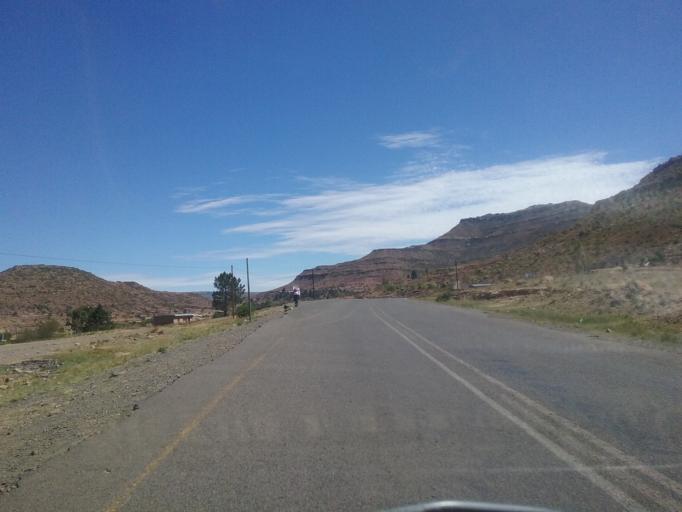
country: LS
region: Quthing
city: Quthing
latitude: -30.3553
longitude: 27.5455
